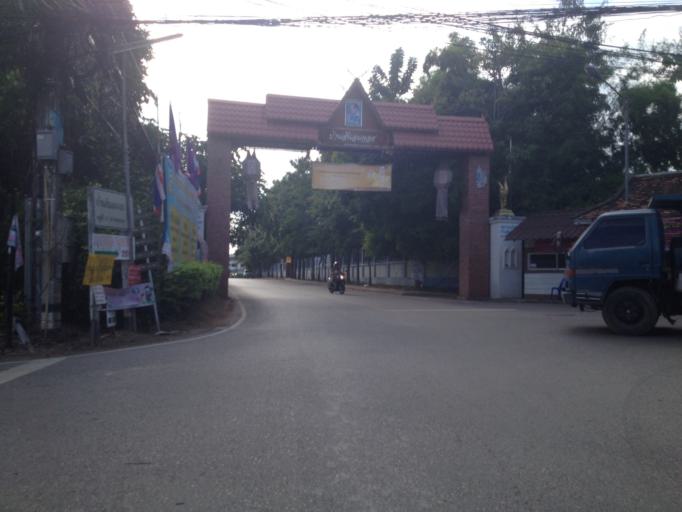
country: TH
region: Chiang Mai
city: Chiang Mai
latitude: 18.7695
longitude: 98.9454
